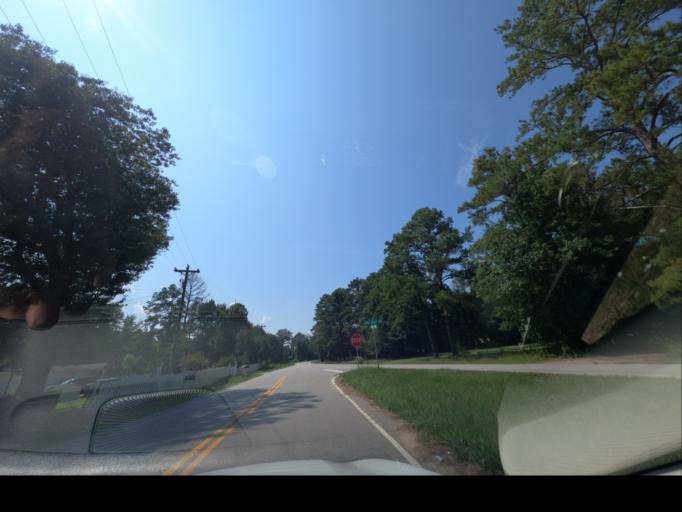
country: US
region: South Carolina
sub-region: Richland County
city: Hopkins
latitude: 33.8667
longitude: -80.8888
